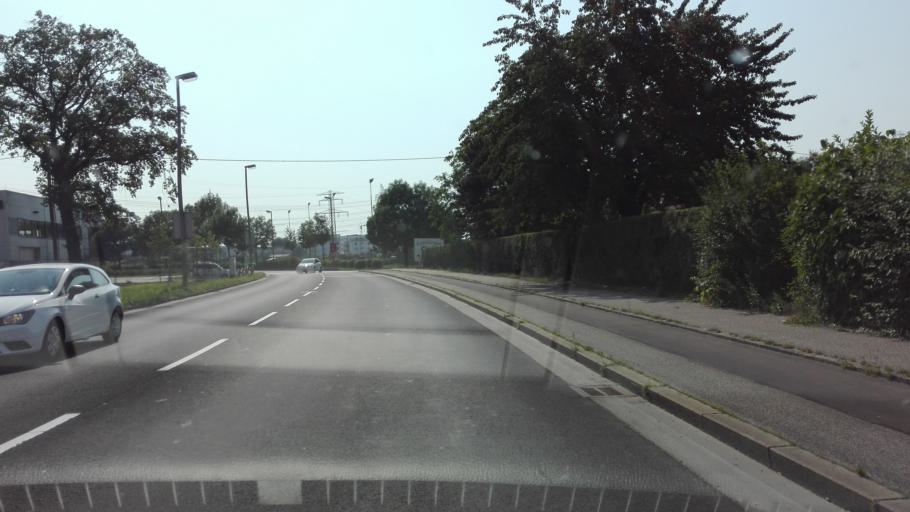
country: AT
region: Upper Austria
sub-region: Politischer Bezirk Linz-Land
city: Ansfelden
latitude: 48.2425
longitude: 14.2881
